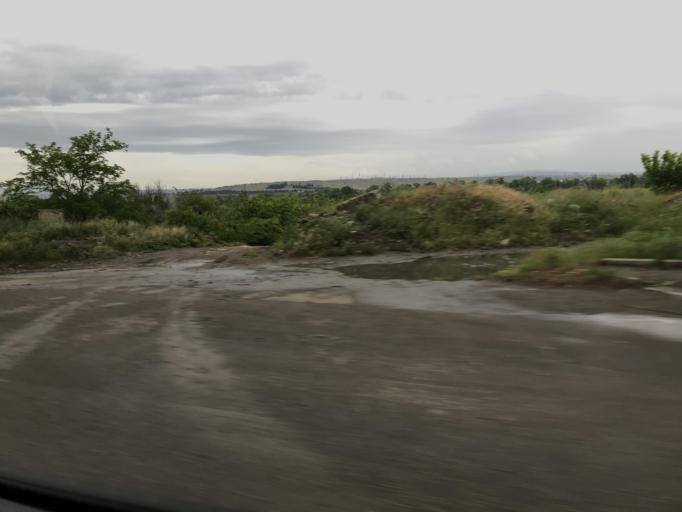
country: GE
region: Kvemo Kartli
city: Rust'avi
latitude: 41.5526
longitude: 44.9917
